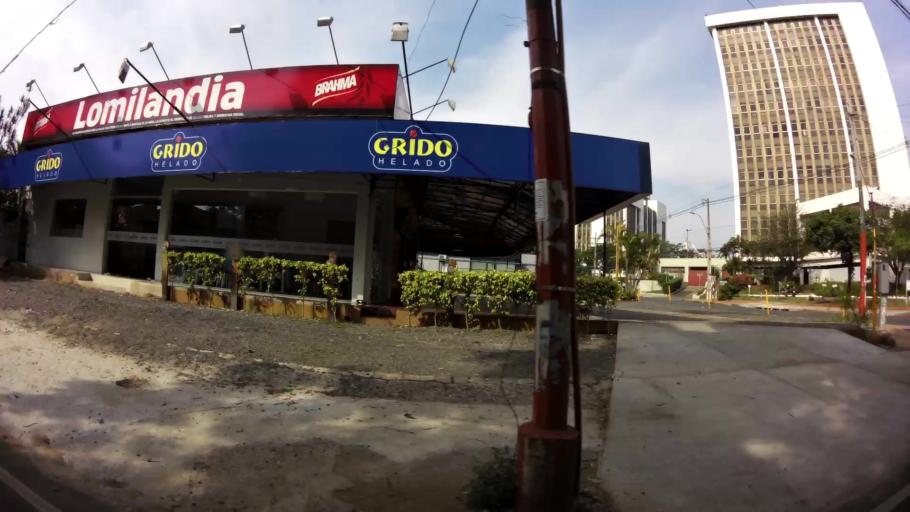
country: PY
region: Central
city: Fernando de la Mora
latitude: -25.3043
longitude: -57.5591
